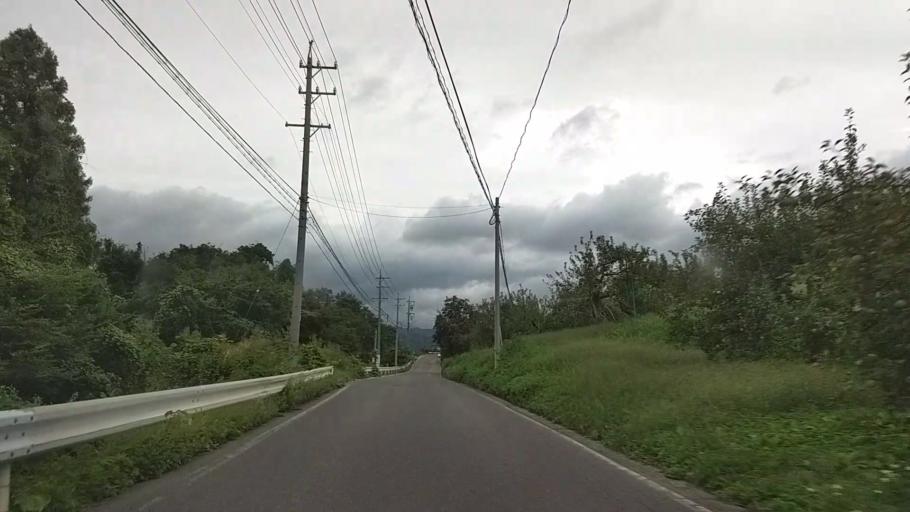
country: JP
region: Nagano
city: Iiyama
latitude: 36.8086
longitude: 138.3606
